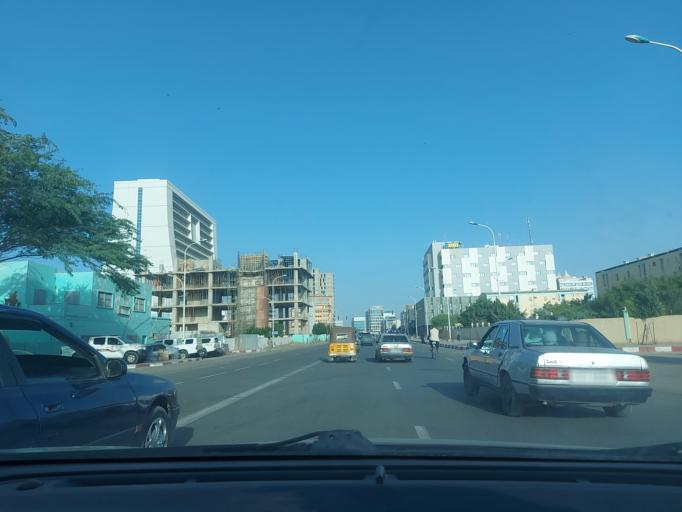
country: MR
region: Nouakchott
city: Nouakchott
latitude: 18.0873
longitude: -15.9736
